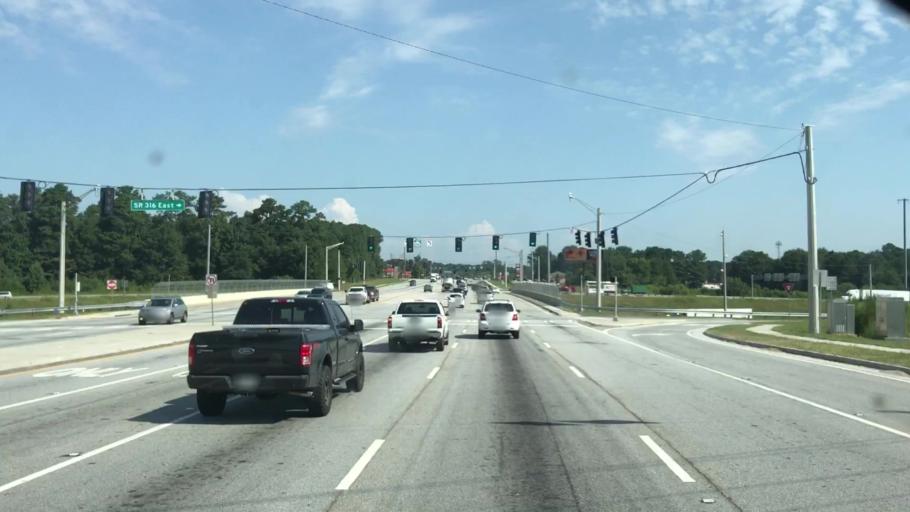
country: US
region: Georgia
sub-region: Gwinnett County
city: Lawrenceville
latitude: 33.9779
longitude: -83.9855
